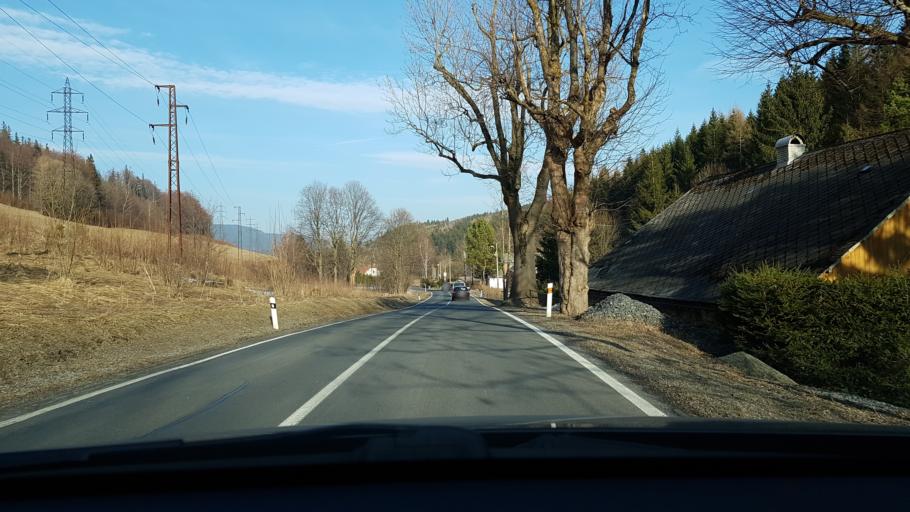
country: CZ
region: Olomoucky
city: Vapenna
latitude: 50.2110
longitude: 17.0948
